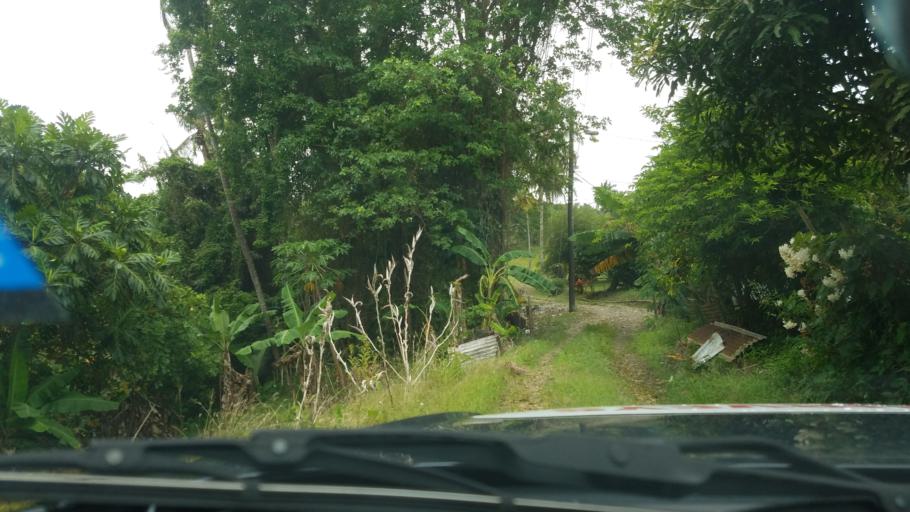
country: LC
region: Gros-Islet
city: Gros Islet
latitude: 14.0259
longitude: -60.9240
